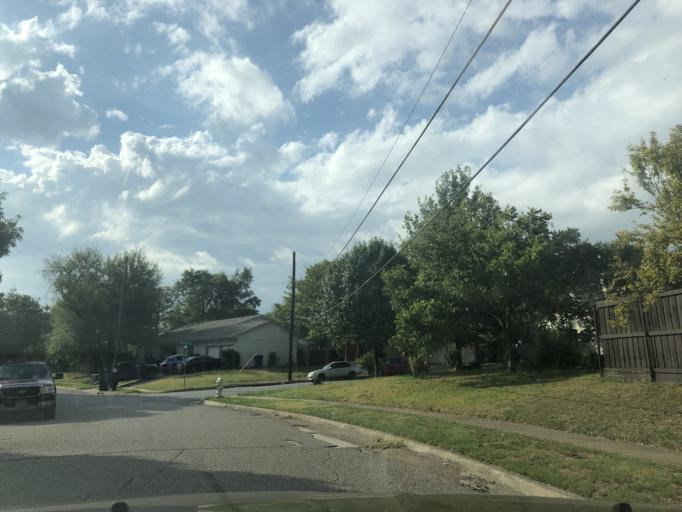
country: US
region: Texas
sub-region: Dallas County
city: Garland
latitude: 32.8849
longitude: -96.6614
